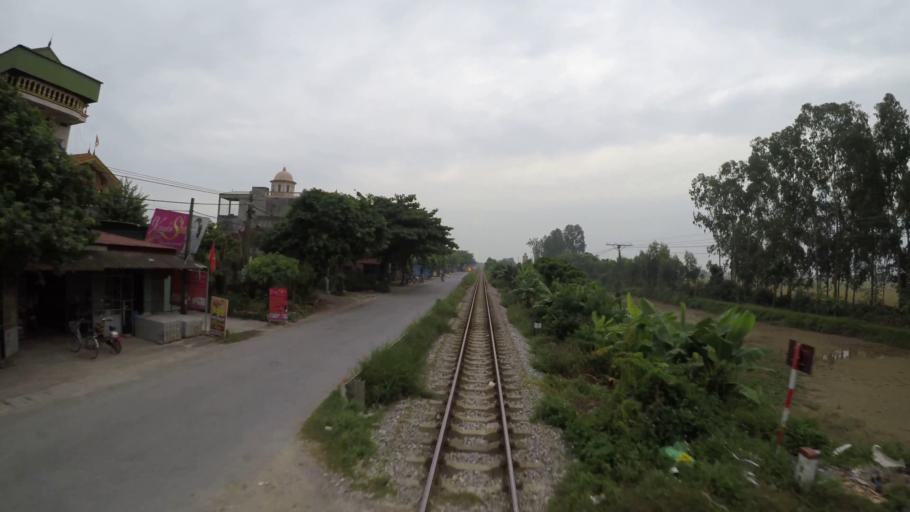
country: VN
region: Hung Yen
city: Ban Yen Nhan
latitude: 20.9674
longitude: 106.1072
